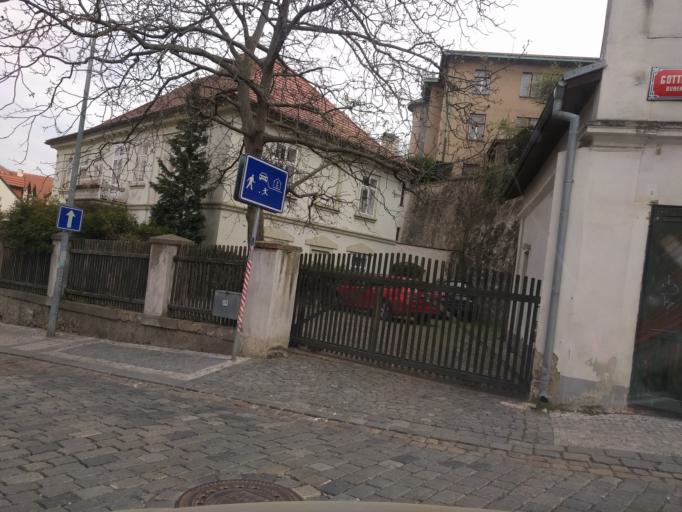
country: CZ
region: Praha
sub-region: Praha 1
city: Mala Strana
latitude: 50.1035
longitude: 14.4087
